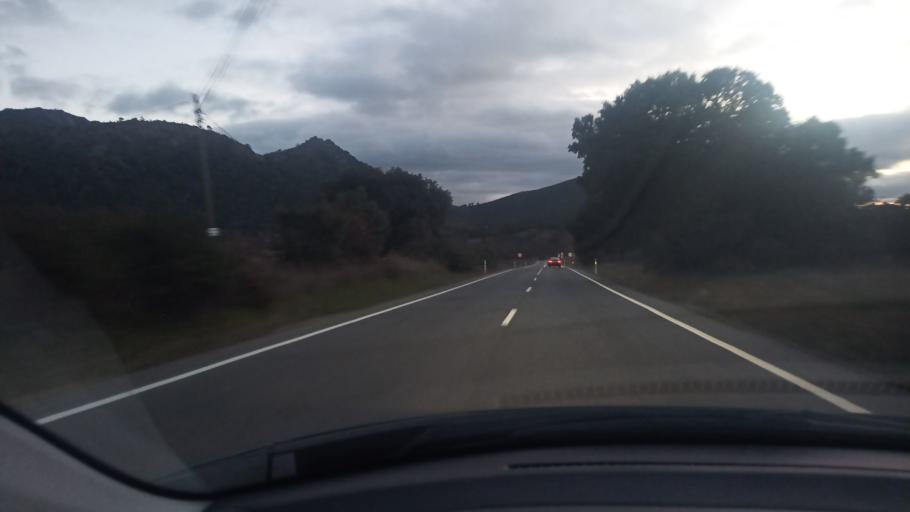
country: ES
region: Madrid
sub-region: Provincia de Madrid
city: Robledo de Chavela
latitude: 40.4760
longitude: -4.2566
